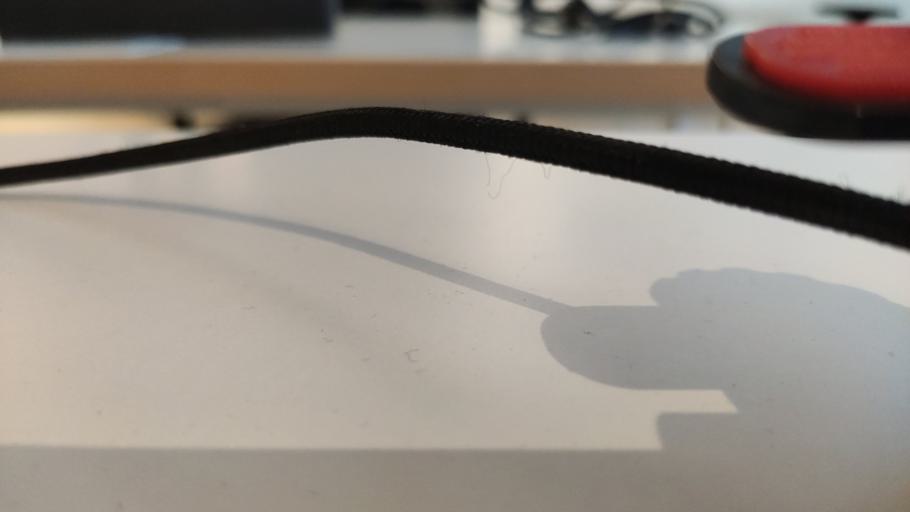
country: RU
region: Moskovskaya
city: Novopetrovskoye
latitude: 55.8839
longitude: 36.4190
